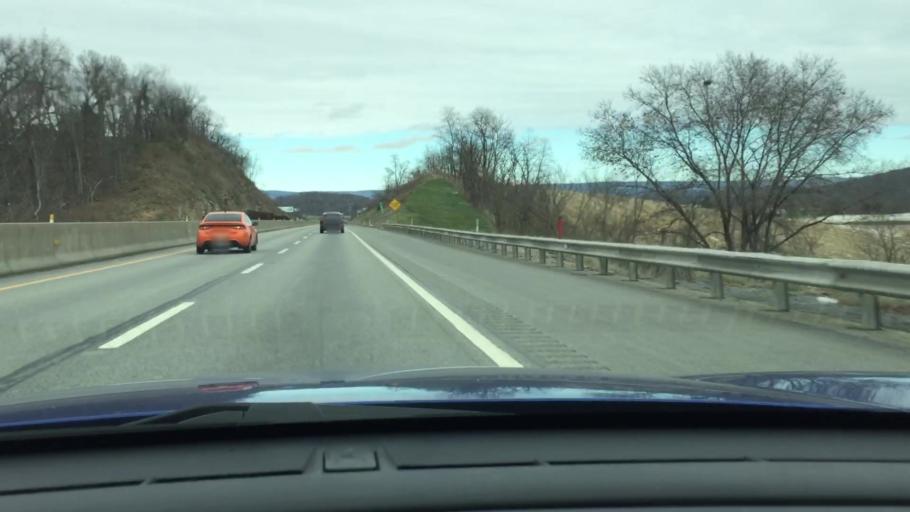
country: US
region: Pennsylvania
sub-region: Bedford County
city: Bedford
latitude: 40.0352
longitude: -78.5694
